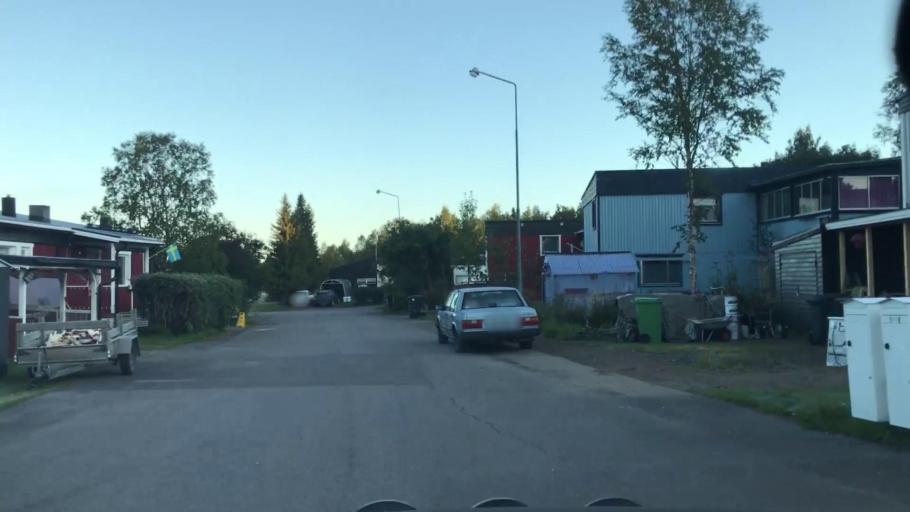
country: SE
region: Norrbotten
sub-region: Gallivare Kommun
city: Malmberget
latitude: 67.6478
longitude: 21.0488
